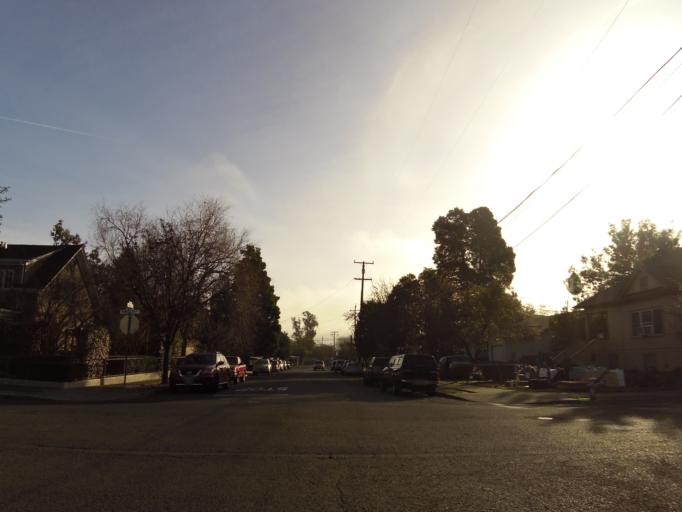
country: US
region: California
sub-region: Napa County
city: Napa
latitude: 38.2878
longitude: -122.2884
